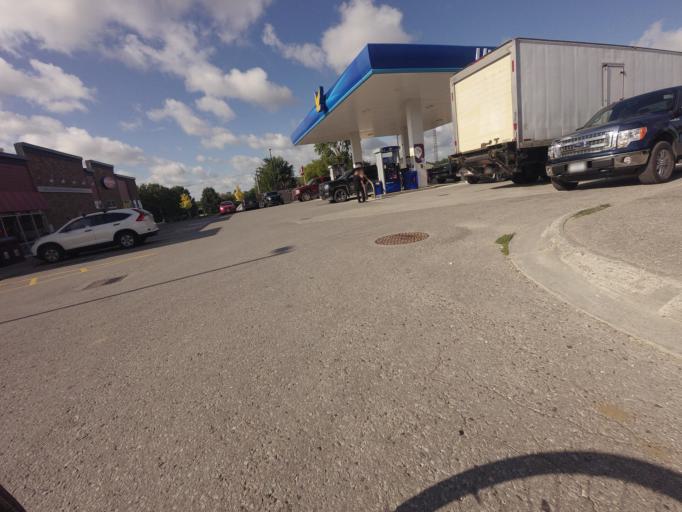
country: CA
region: Ontario
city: Huron East
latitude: 43.7314
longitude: -81.4343
